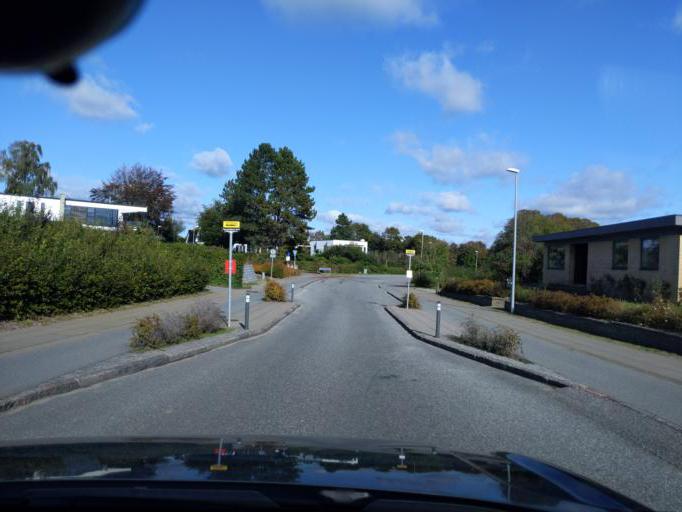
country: DK
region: Central Jutland
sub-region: Viborg Kommune
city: Viborg
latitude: 56.4680
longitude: 9.4253
